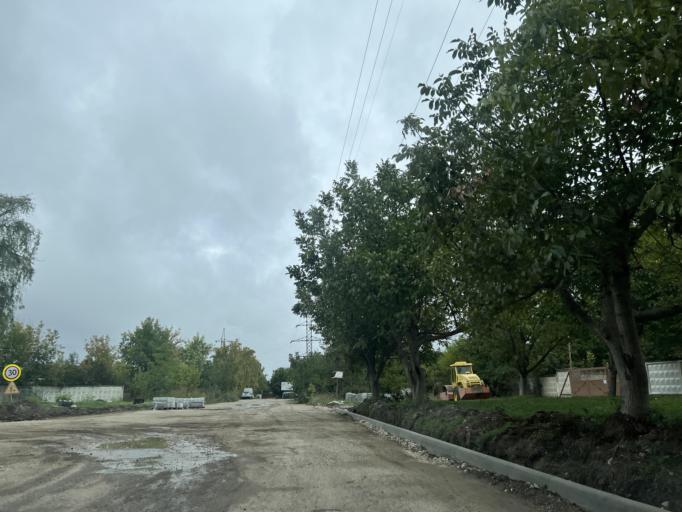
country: MD
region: Ungheni
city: Ungheni
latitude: 47.2251
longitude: 27.8060
